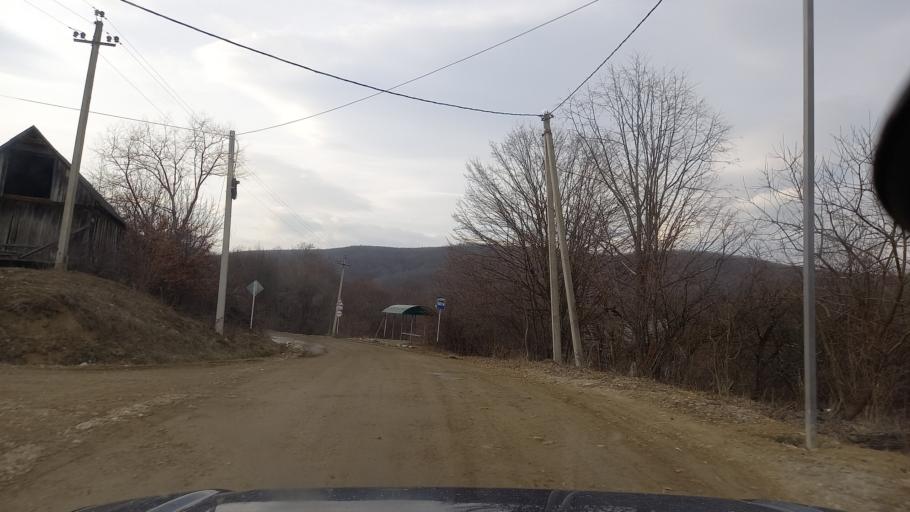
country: RU
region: Adygeya
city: Kamennomostskiy
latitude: 44.1392
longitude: 40.2861
